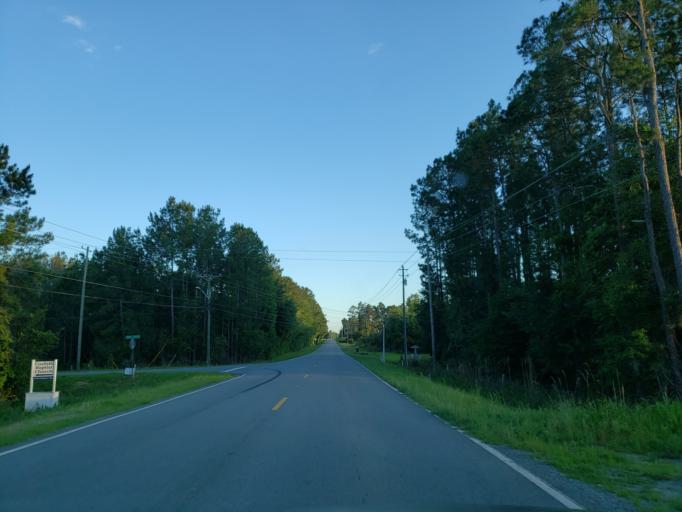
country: US
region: Georgia
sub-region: Lowndes County
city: Valdosta
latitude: 30.7110
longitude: -83.2422
